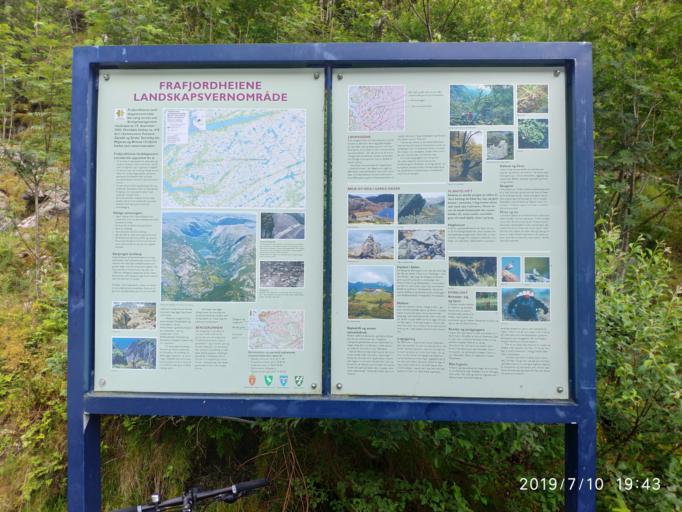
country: NO
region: Rogaland
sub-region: Forsand
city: Forsand
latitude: 58.8589
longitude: 6.3789
